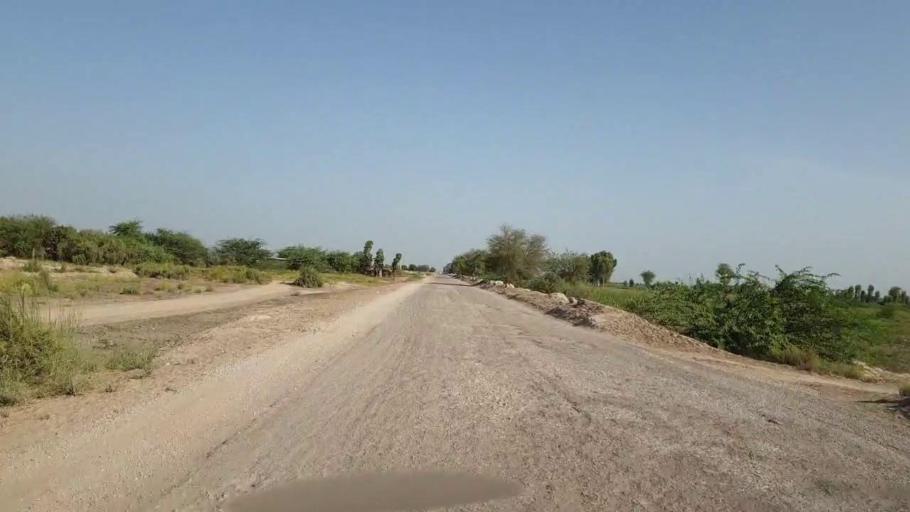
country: PK
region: Sindh
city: Nawabshah
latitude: 26.1611
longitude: 68.4438
